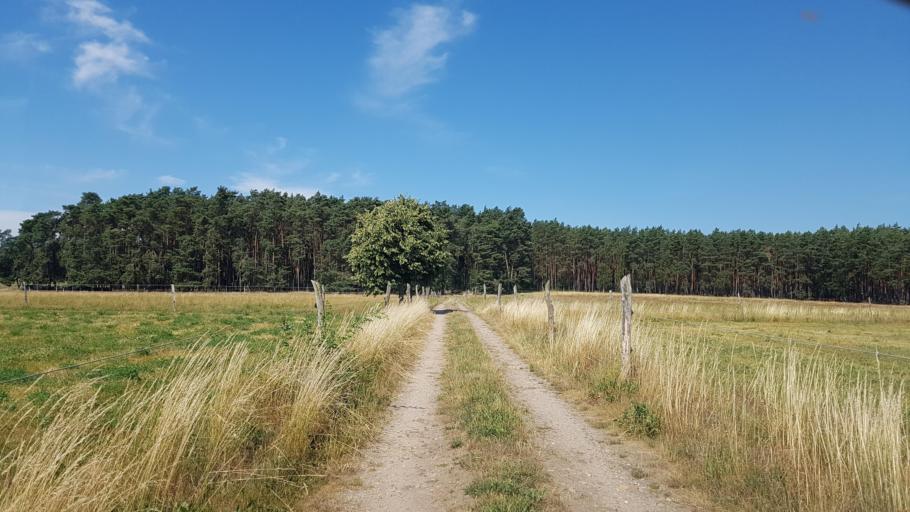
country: DE
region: Brandenburg
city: Altdobern
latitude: 51.6728
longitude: 13.9793
